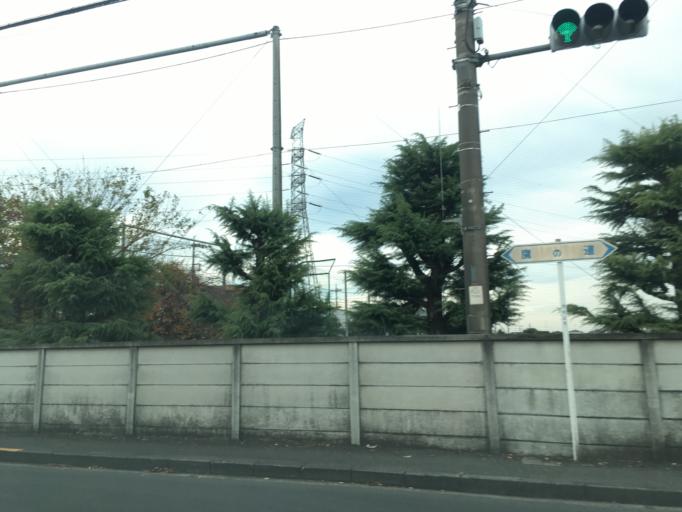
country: JP
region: Tokyo
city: Higashimurayama-shi
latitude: 35.7555
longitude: 139.4578
